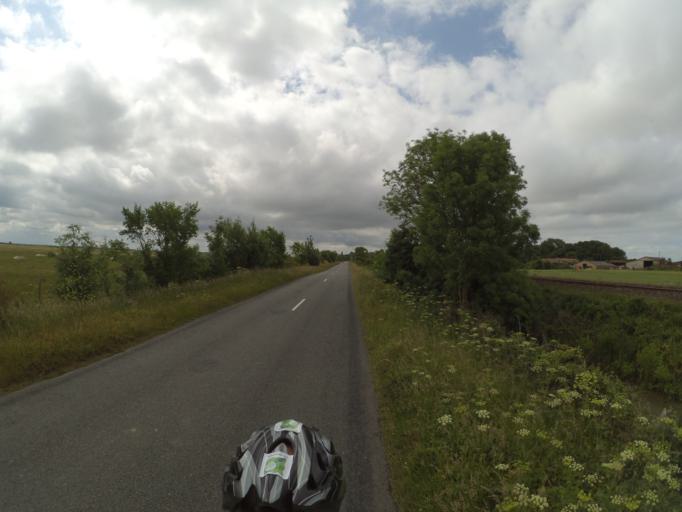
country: FR
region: Poitou-Charentes
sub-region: Departement de la Charente-Maritime
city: Yves
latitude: 46.0255
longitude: -1.0474
